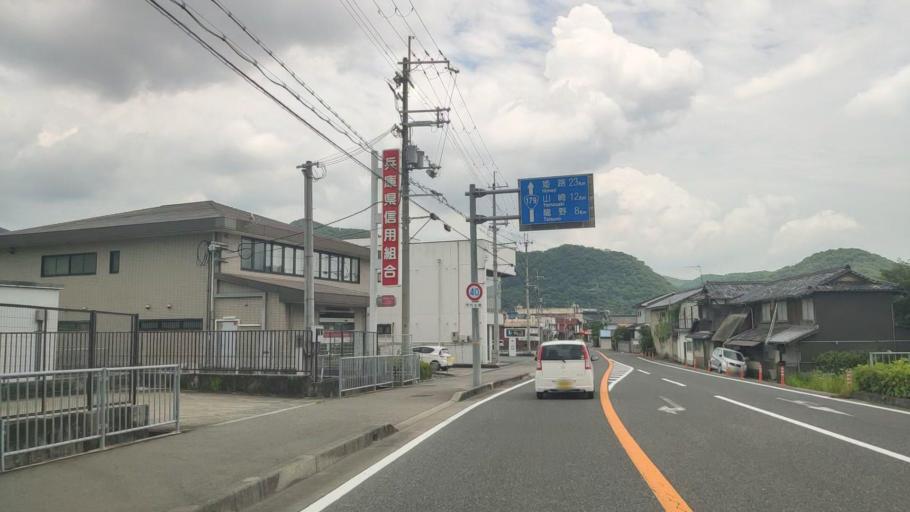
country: JP
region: Hyogo
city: Tatsunocho-tominaga
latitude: 34.9208
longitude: 134.5434
